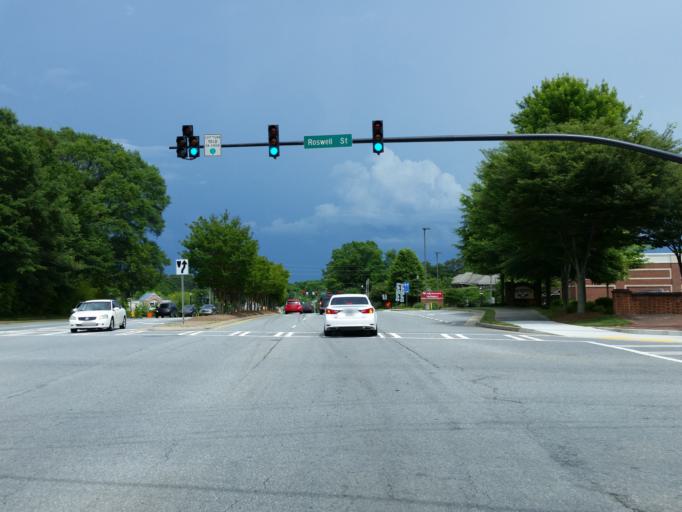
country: US
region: Georgia
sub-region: Fulton County
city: Alpharetta
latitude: 34.0715
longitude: -84.2988
